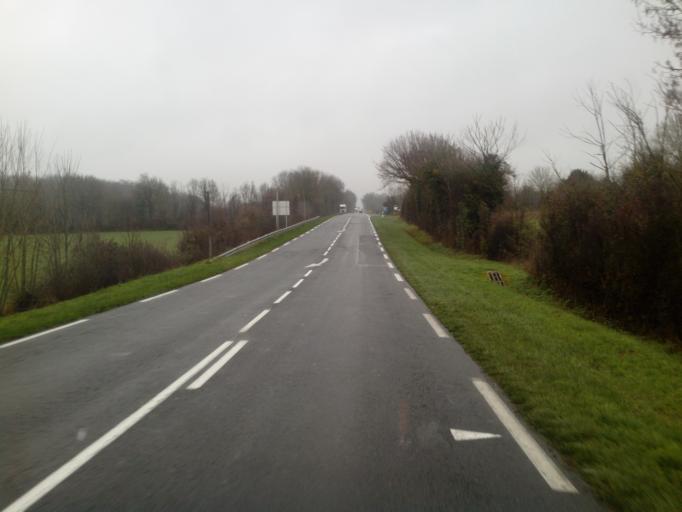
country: FR
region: Poitou-Charentes
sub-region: Departement de la Vienne
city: Terce
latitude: 46.4383
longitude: 0.5905
